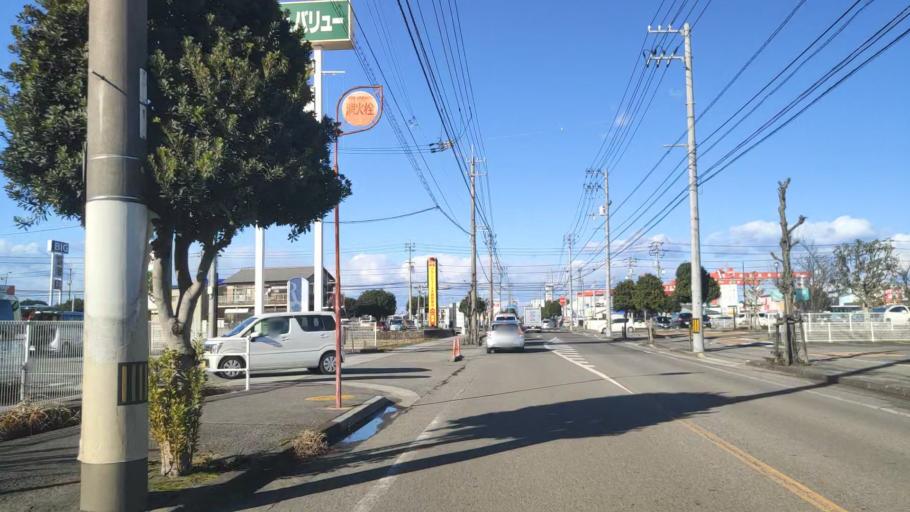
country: JP
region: Ehime
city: Saijo
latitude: 33.9283
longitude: 133.1904
